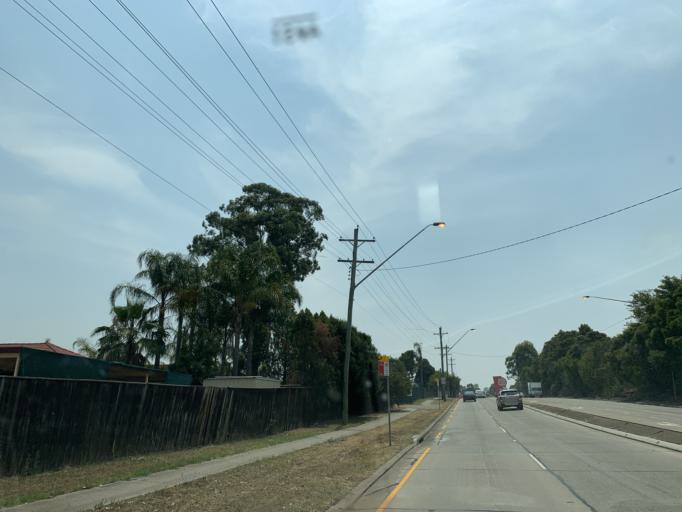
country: AU
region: New South Wales
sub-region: Blacktown
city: Glendenning
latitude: -33.7382
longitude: 150.8560
